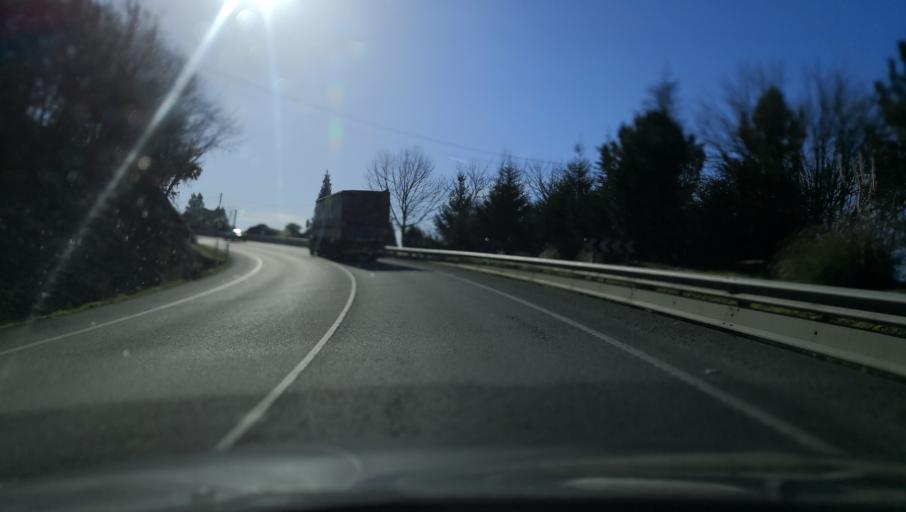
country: ES
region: Galicia
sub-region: Provincia da Coruna
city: Vedra
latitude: 42.8004
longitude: -8.4774
